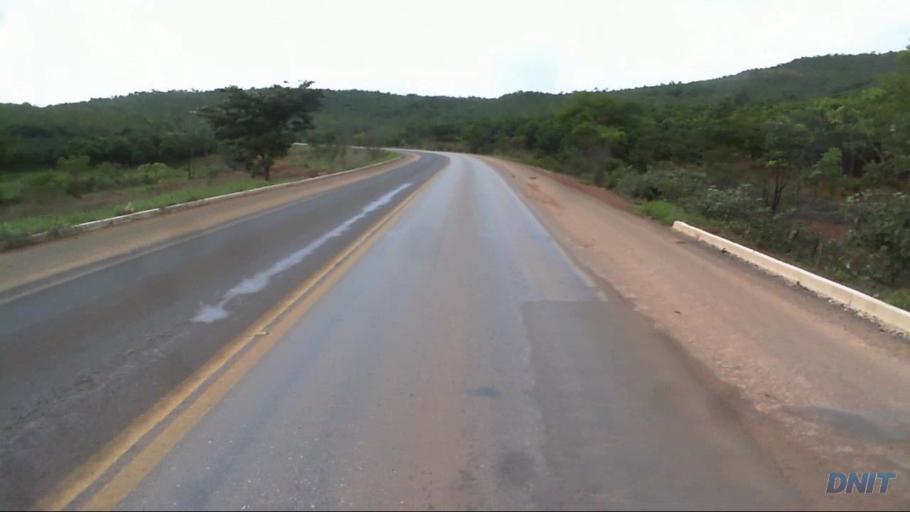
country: BR
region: Goias
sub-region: Barro Alto
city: Barro Alto
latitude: -14.9306
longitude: -48.9491
